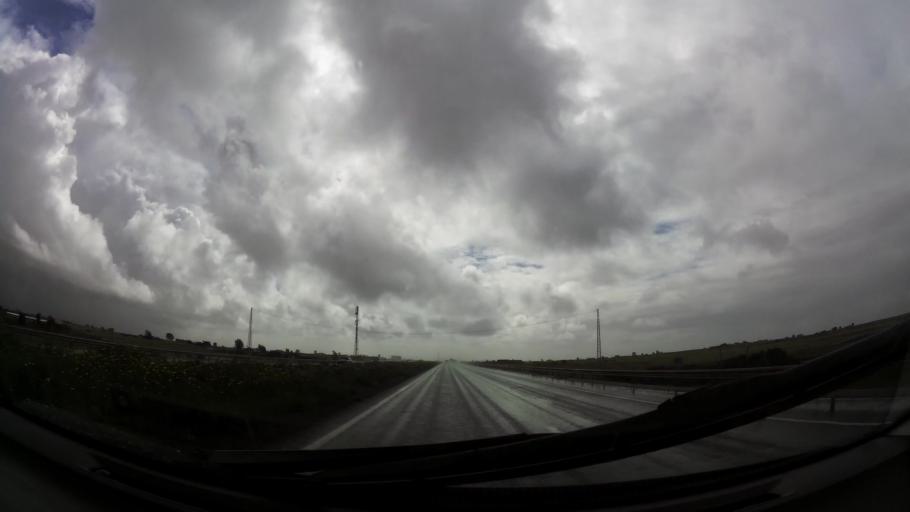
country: MA
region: Grand Casablanca
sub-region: Nouaceur
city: Dar Bouazza
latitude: 33.3927
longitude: -7.8616
